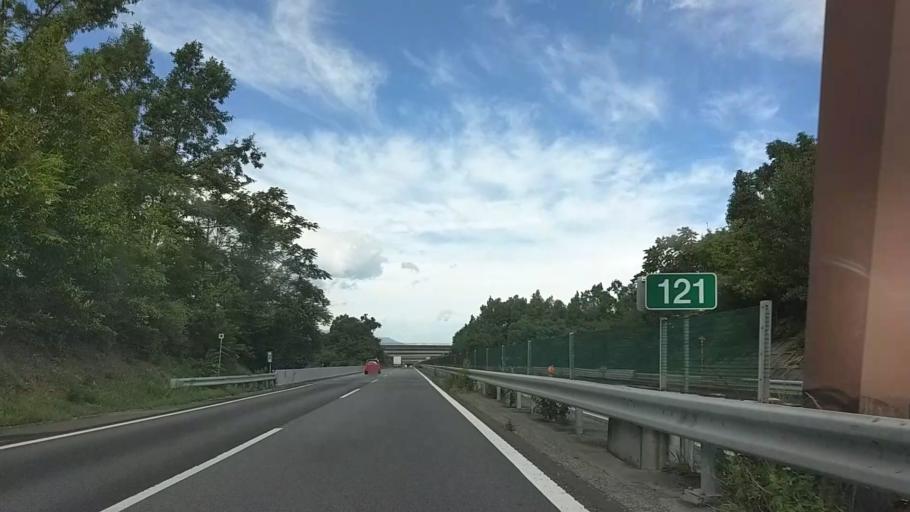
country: JP
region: Yamanashi
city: Nirasaki
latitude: 35.6967
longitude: 138.4873
